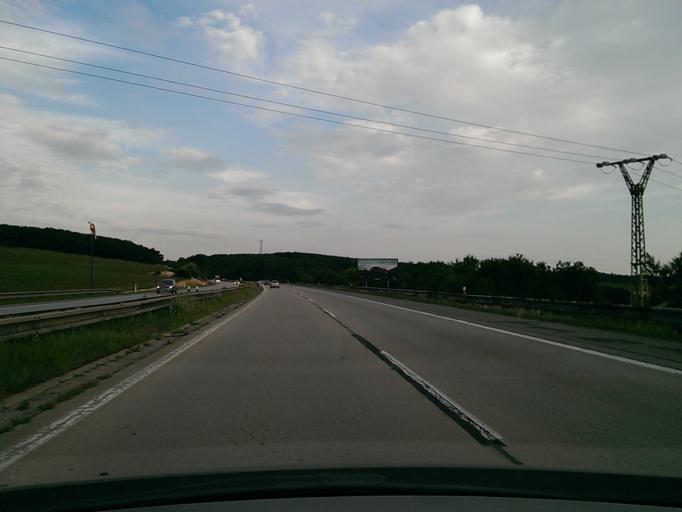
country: CZ
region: South Moravian
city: Ricany
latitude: 49.2017
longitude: 16.4221
